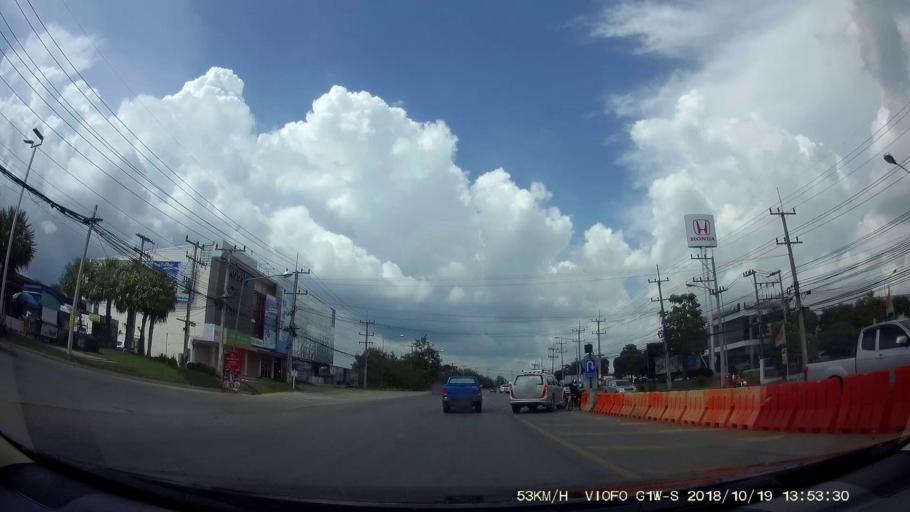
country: TH
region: Chaiyaphum
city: Chaiyaphum
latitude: 15.7780
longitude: 102.0253
